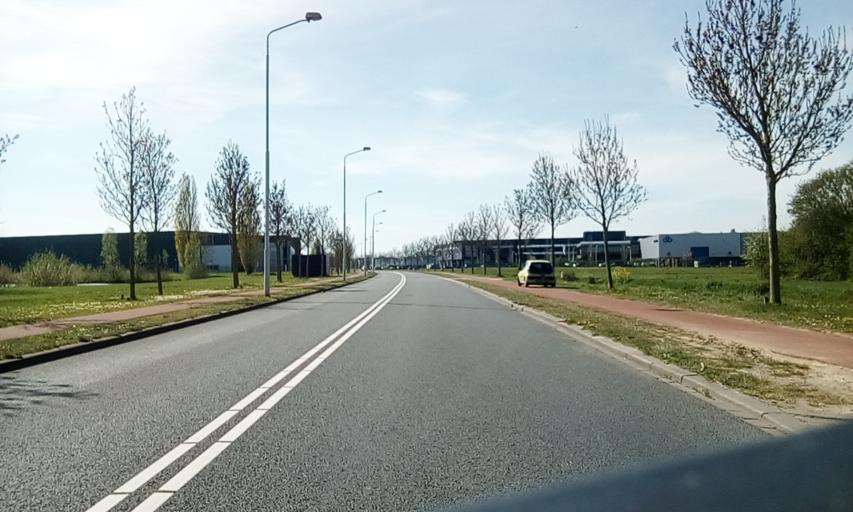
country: NL
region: Gelderland
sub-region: Gemeente Beuningen
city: Beuningen
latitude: 51.8305
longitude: 5.7536
